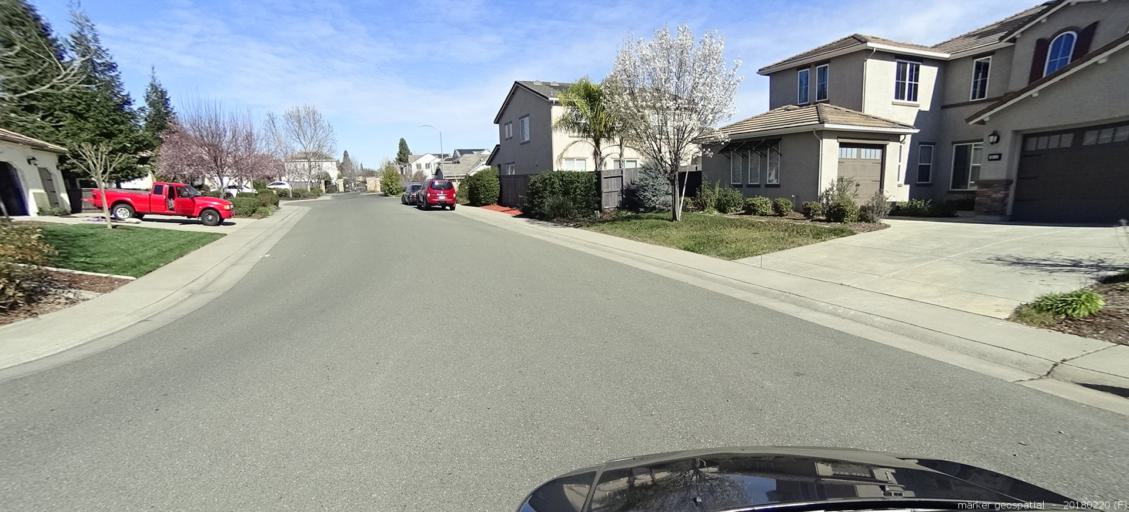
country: US
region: California
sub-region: Sacramento County
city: Orangevale
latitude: 38.6756
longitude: -121.2204
